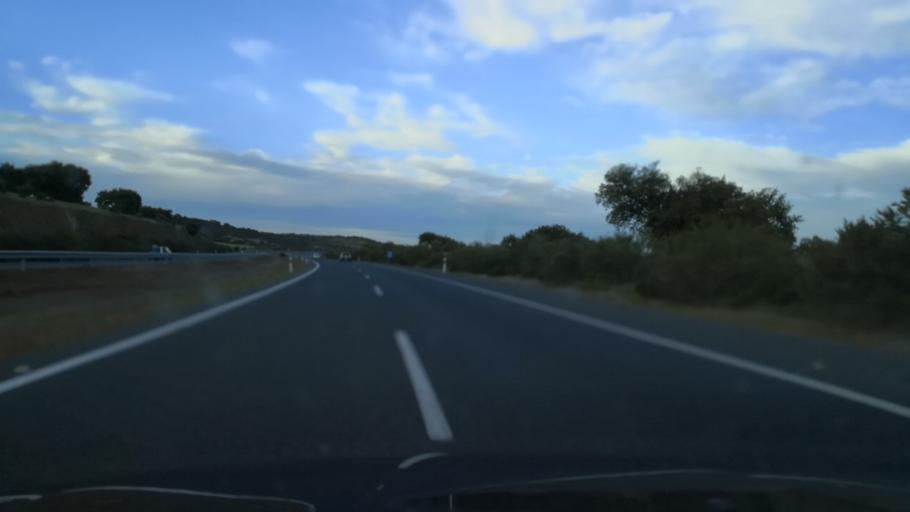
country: ES
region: Extremadura
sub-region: Provincia de Badajoz
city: Aljucen
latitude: 39.0563
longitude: -6.3241
